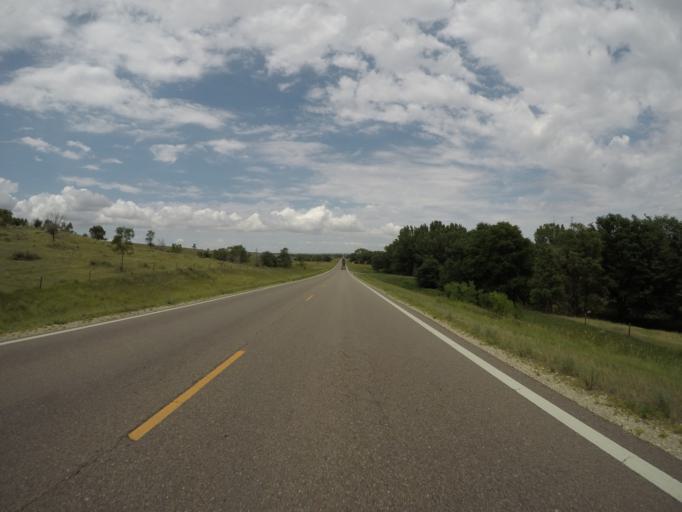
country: US
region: Kansas
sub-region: Rawlins County
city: Atwood
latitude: 39.7911
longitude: -101.0469
